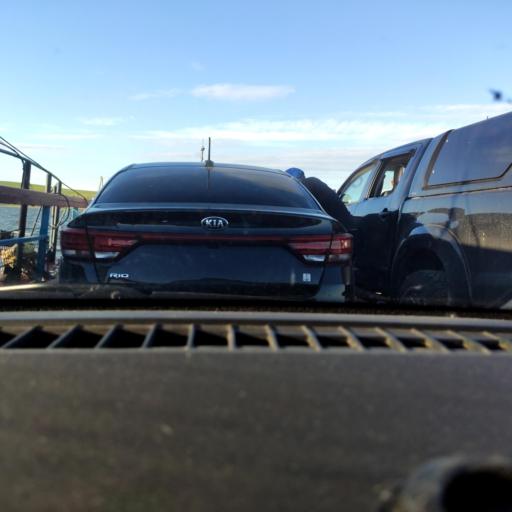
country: RU
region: Perm
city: Verkhnechusovskiye Gorodki
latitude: 58.1891
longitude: 57.1246
